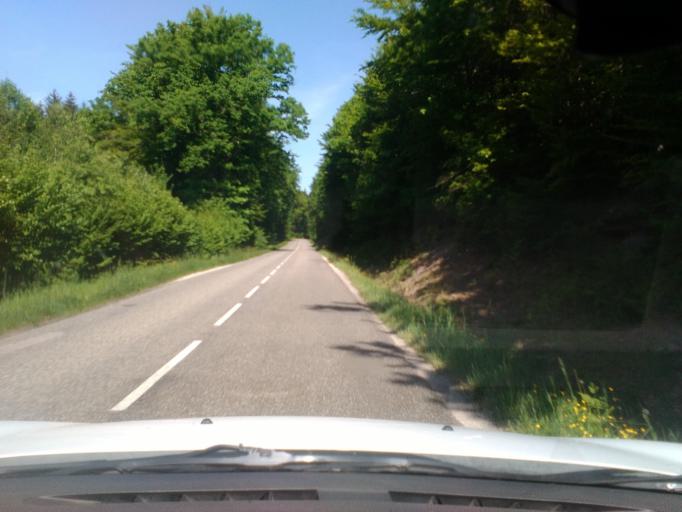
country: FR
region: Lorraine
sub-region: Departement des Vosges
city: Jeanmenil
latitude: 48.2813
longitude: 6.7051
